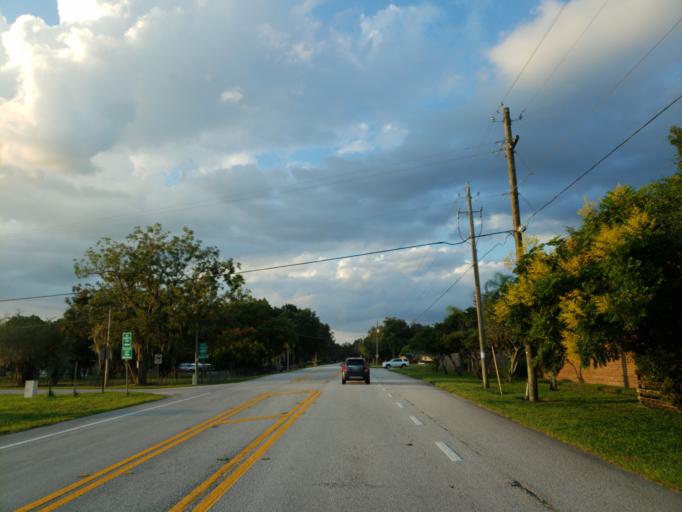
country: US
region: Florida
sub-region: Pasco County
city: Odessa
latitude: 28.1654
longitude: -82.5891
